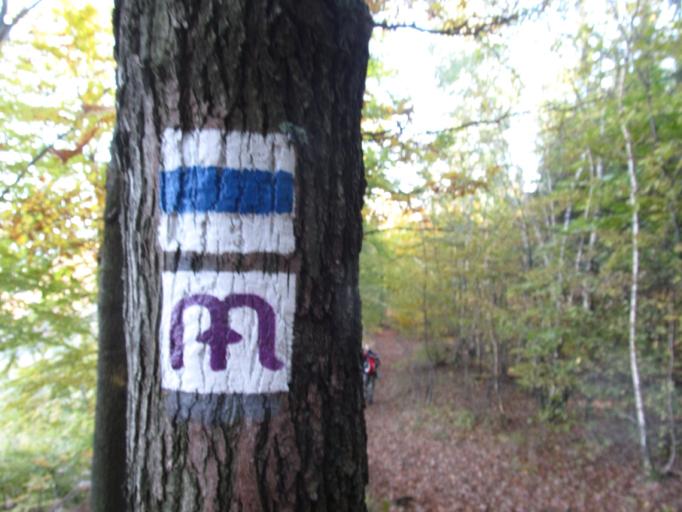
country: HU
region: Heves
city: Paradsasvar
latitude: 47.9090
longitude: 19.9473
